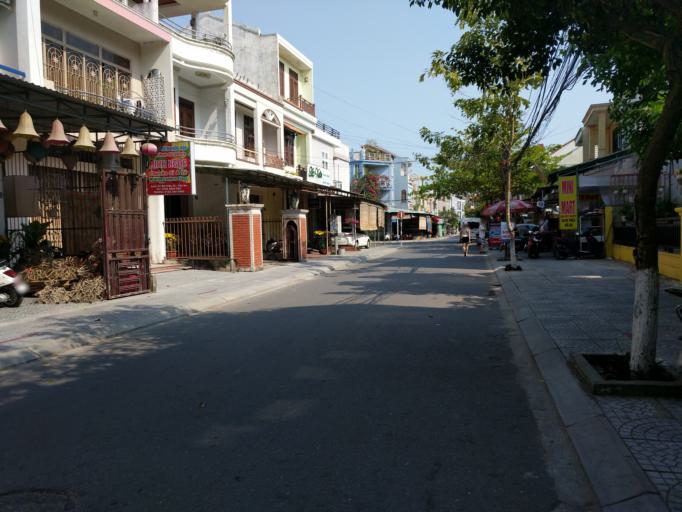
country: VN
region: Quang Nam
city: Hoi An
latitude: 15.8818
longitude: 108.3249
